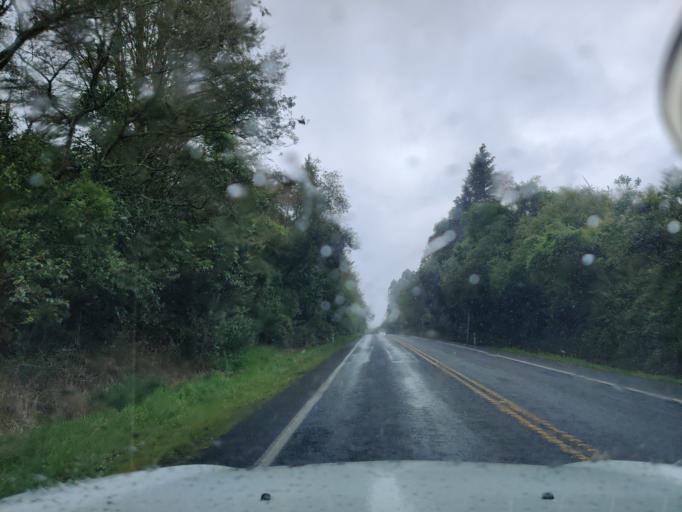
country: NZ
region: Bay of Plenty
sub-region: Rotorua District
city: Rotorua
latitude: -38.0813
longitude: 176.1865
